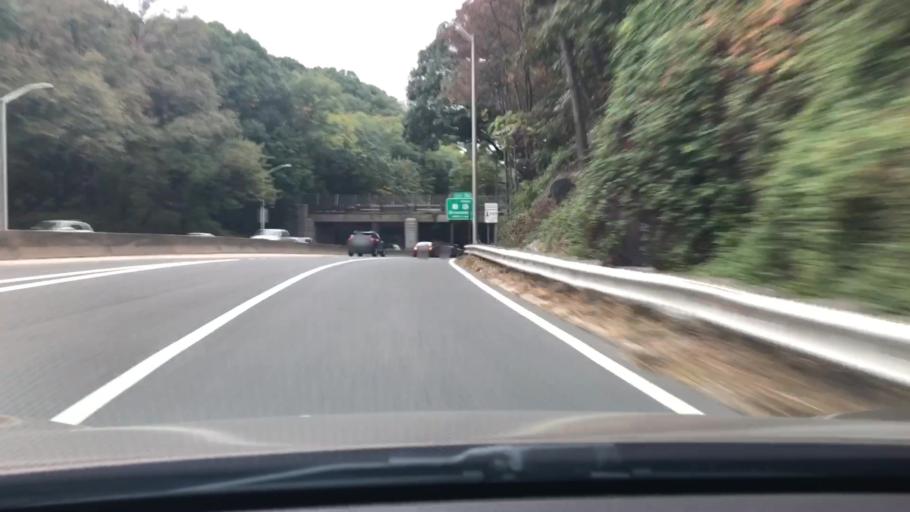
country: US
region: New York
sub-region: Westchester County
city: Yonkers
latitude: 40.9000
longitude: -73.8908
